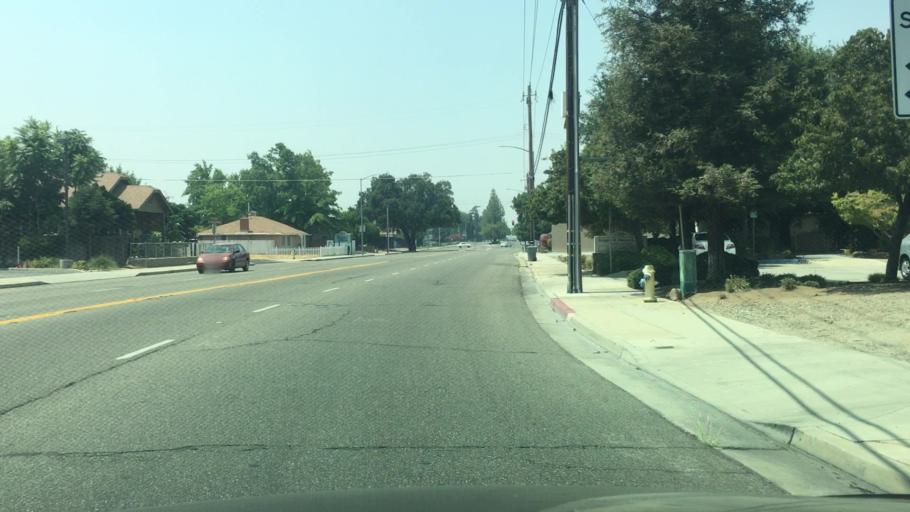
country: US
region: California
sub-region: Fresno County
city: Clovis
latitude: 36.8231
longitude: -119.7062
